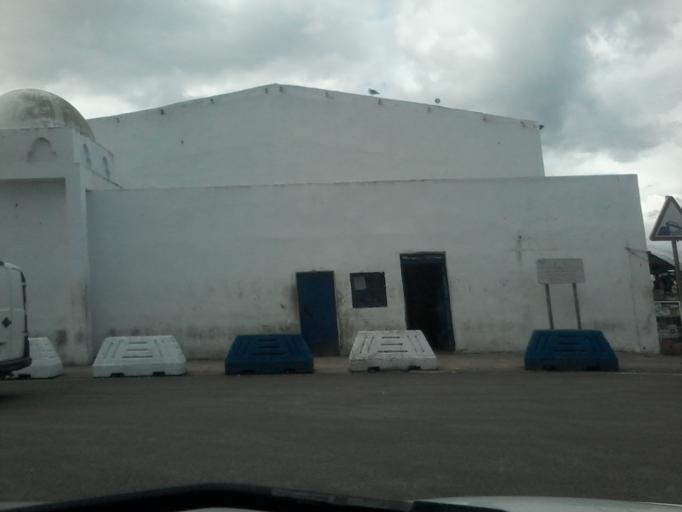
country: MA
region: Tanger-Tetouan
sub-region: Tetouan
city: Martil
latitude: 35.6814
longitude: -5.3110
